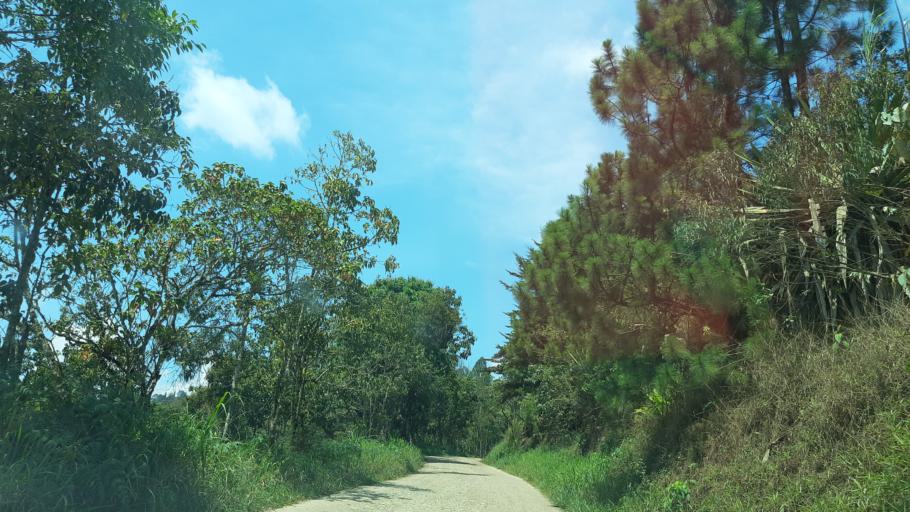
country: CO
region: Boyaca
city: Chinavita
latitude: 5.1291
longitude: -73.3745
